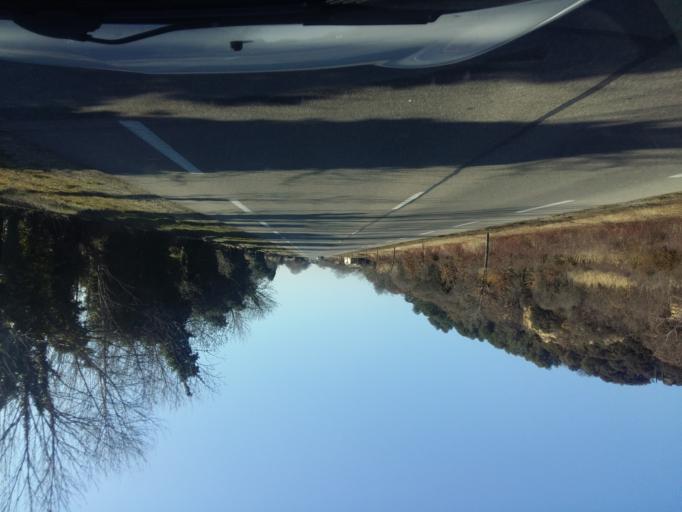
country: FR
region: Provence-Alpes-Cote d'Azur
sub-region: Departement du Vaucluse
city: Lauris
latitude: 43.7417
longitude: 5.3208
